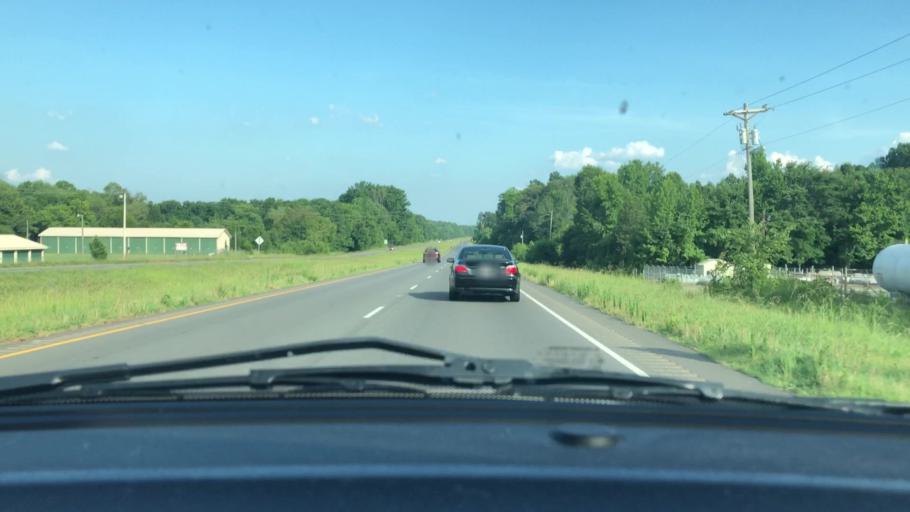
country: US
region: North Carolina
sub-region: Chatham County
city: Siler City
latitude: 35.6519
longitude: -79.3915
